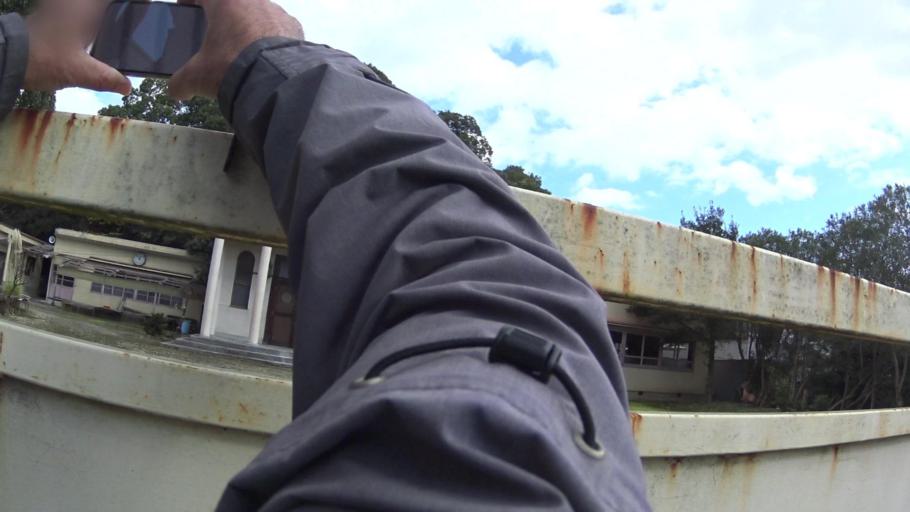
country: JP
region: Kyoto
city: Uji
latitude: 34.9552
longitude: 135.7806
